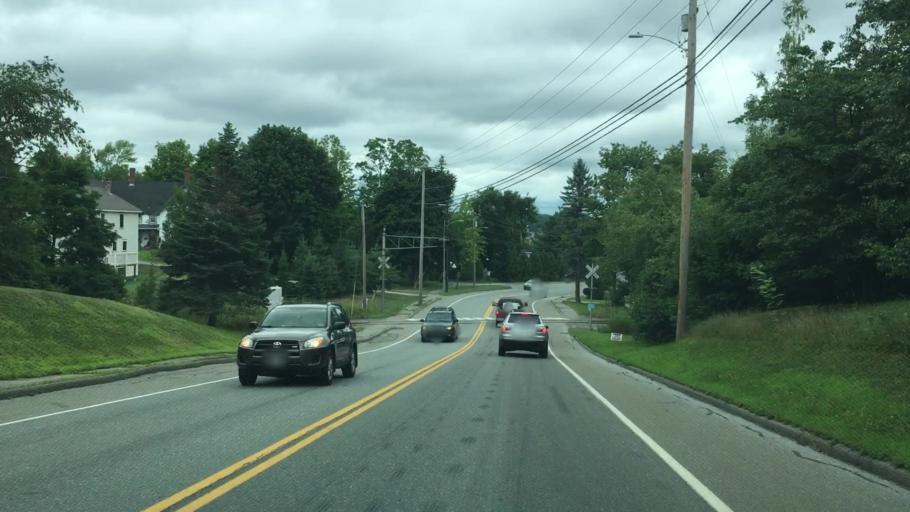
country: US
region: Maine
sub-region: Penobscot County
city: Bangor
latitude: 44.7664
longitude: -68.7835
